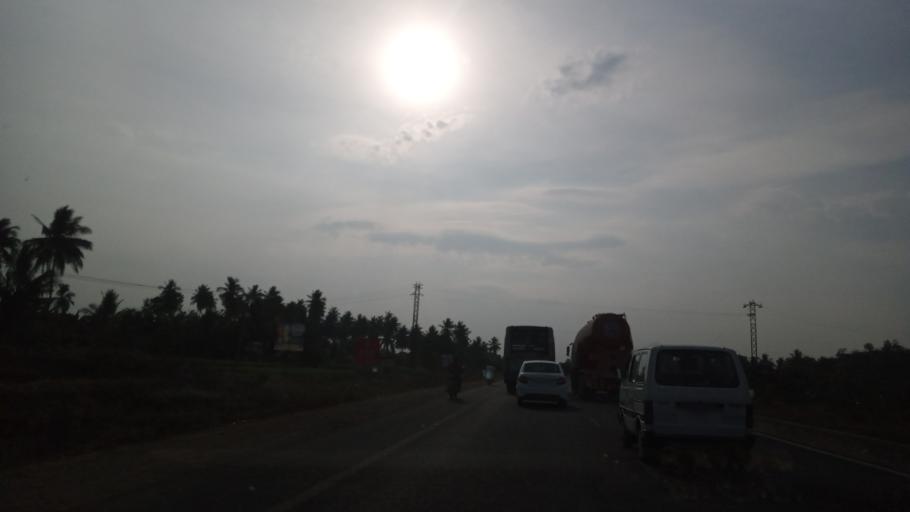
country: IN
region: Tamil Nadu
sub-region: Salem
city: Belur
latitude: 11.6523
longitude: 78.4625
